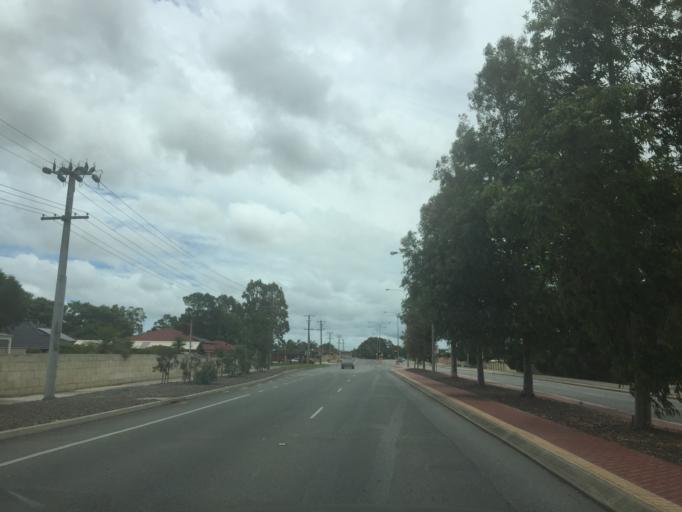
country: AU
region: Western Australia
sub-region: Gosnells
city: Thornlie
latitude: -32.0766
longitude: 115.9451
